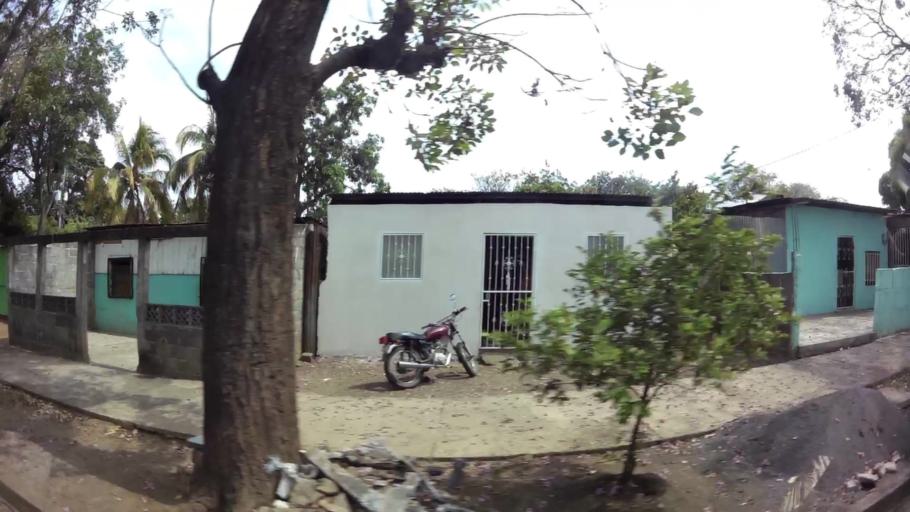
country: NI
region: Managua
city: Managua
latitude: 12.1516
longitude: -86.2812
